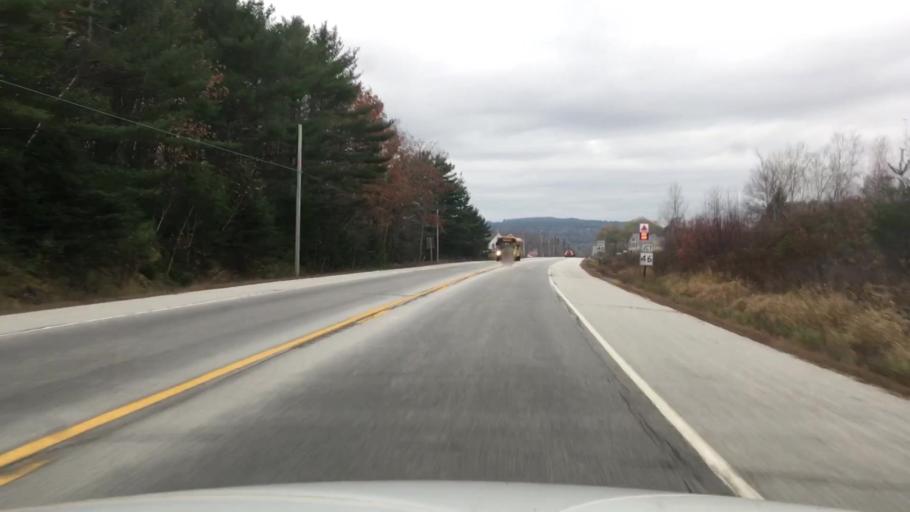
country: US
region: Maine
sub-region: Hancock County
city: Orland
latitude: 44.5705
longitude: -68.7616
